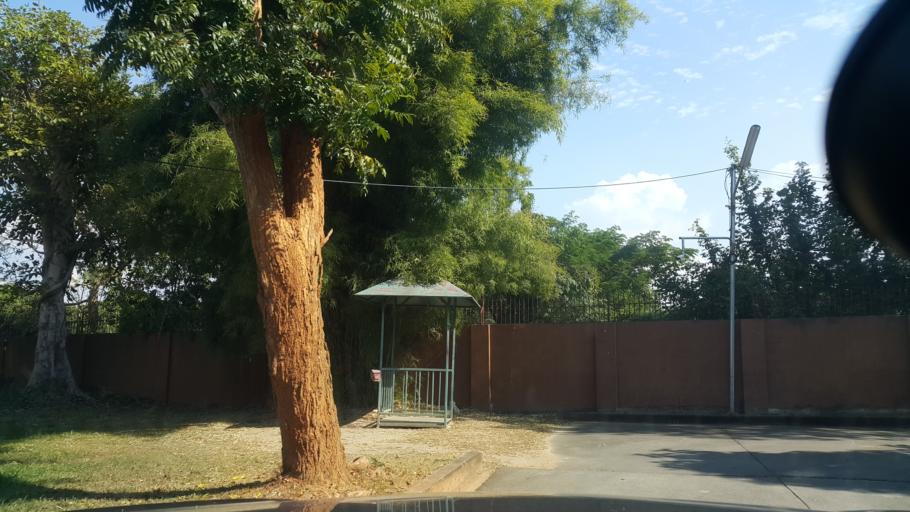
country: TH
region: Chiang Mai
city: Hang Dong
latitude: 18.7301
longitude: 98.9468
